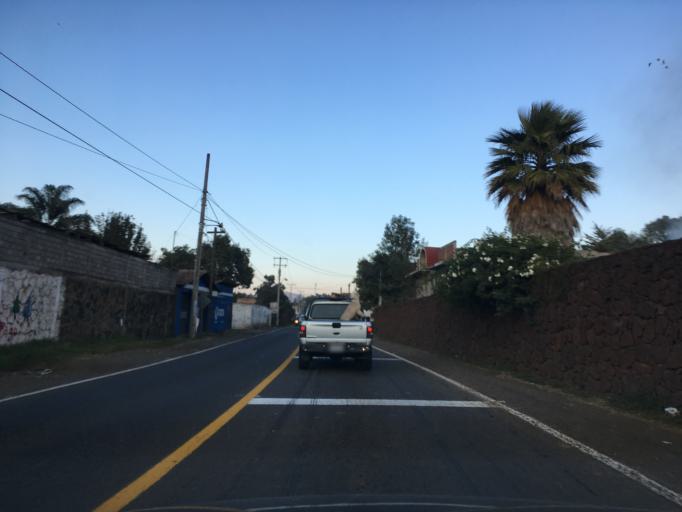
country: MX
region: Michoacan
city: Patzcuaro
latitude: 19.5325
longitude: -101.6187
